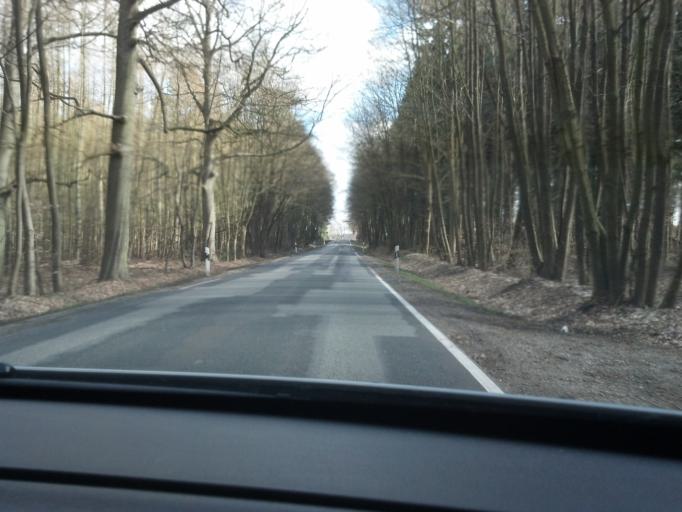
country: DE
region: Schleswig-Holstein
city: Langenlehsten
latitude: 53.4830
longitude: 10.8155
